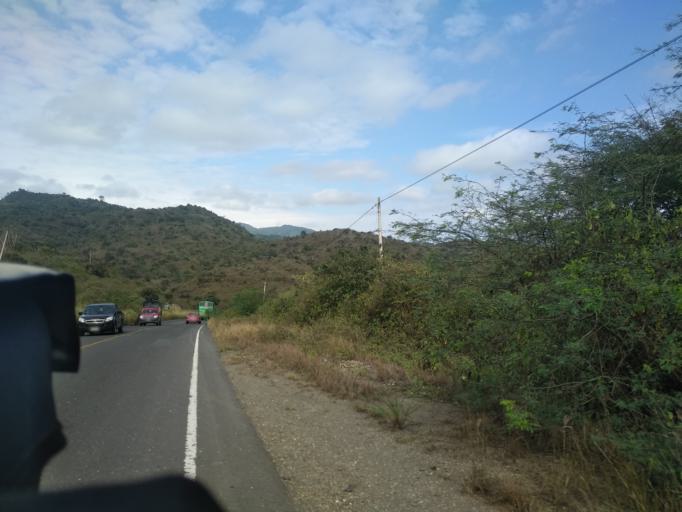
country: EC
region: Manabi
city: Jipijapa
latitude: -1.4387
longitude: -80.7555
